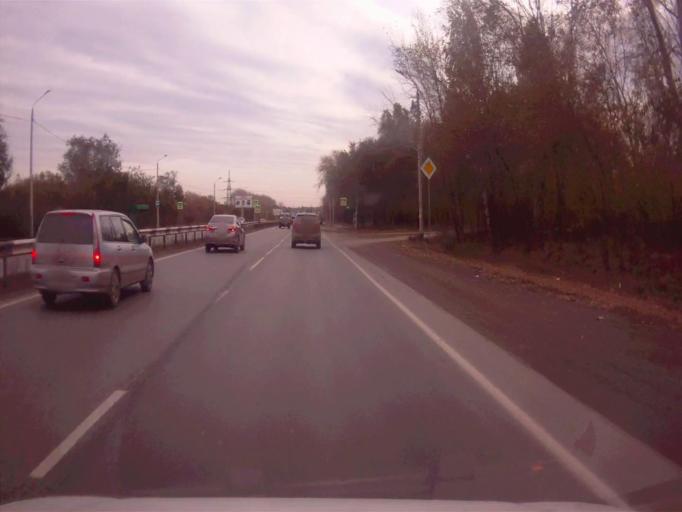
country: RU
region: Chelyabinsk
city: Novosineglazovskiy
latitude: 55.0525
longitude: 61.4107
